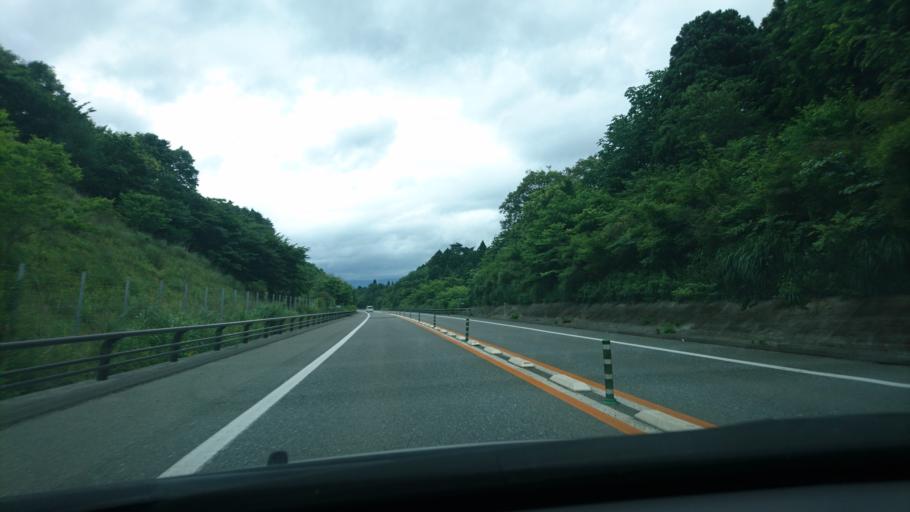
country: JP
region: Iwate
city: Ofunato
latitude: 39.0455
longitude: 141.7155
